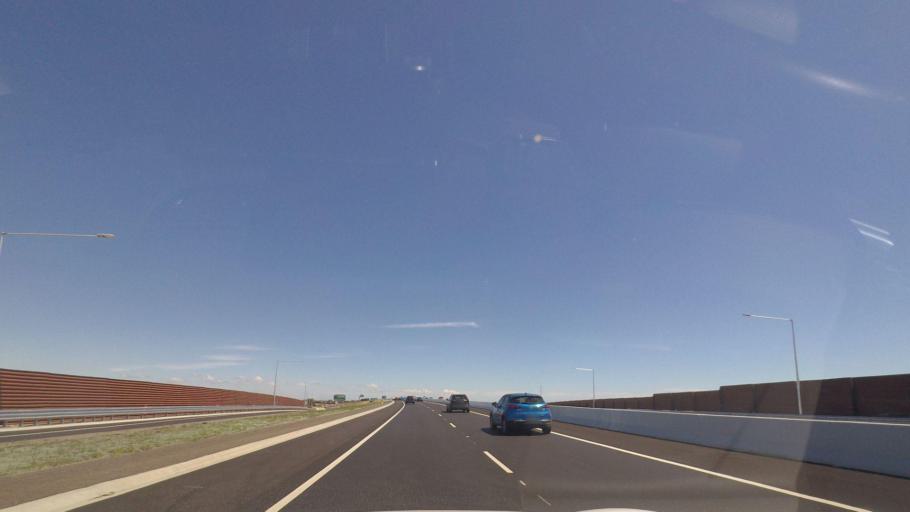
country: AU
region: Victoria
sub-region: Kingston
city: Waterways
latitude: -38.0058
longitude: 145.1227
